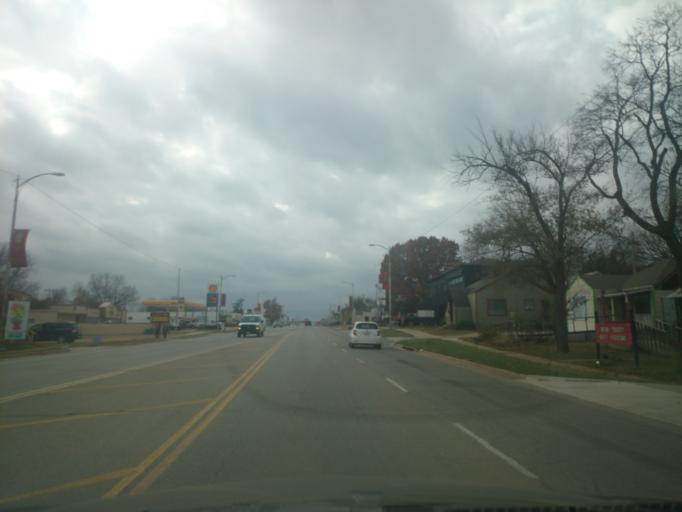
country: US
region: Oklahoma
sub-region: Payne County
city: Stillwater
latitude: 36.1230
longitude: -97.0588
